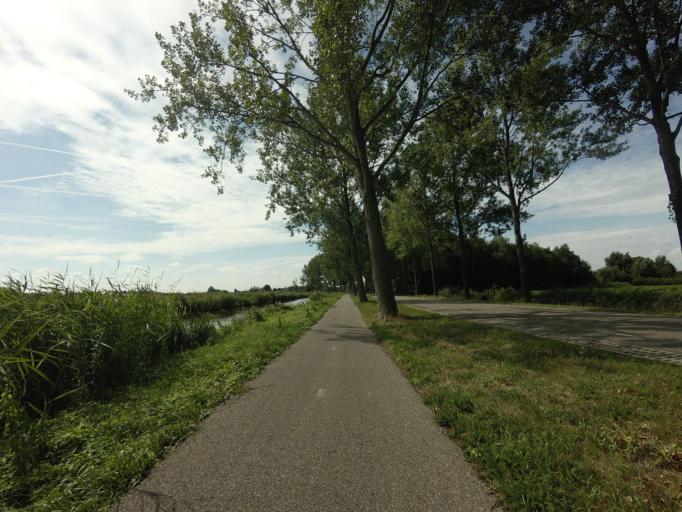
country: NL
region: North Holland
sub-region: Gemeente Uithoorn
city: Uithoorn
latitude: 52.2127
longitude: 4.8201
